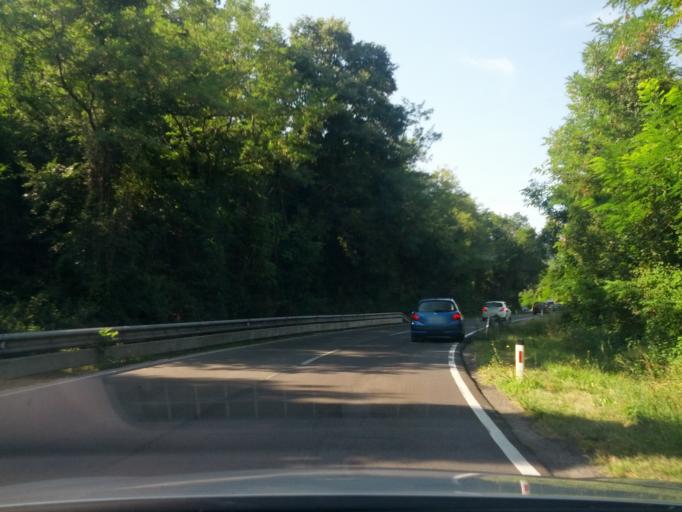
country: SI
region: Izola-Isola
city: Jagodje
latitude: 45.4779
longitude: 13.6756
